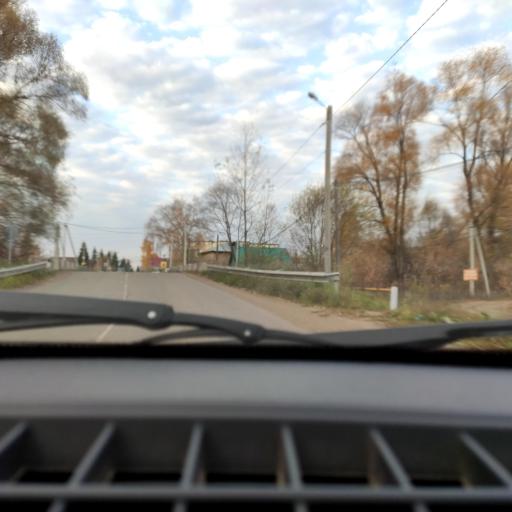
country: RU
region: Bashkortostan
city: Avdon
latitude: 54.6563
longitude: 55.7664
